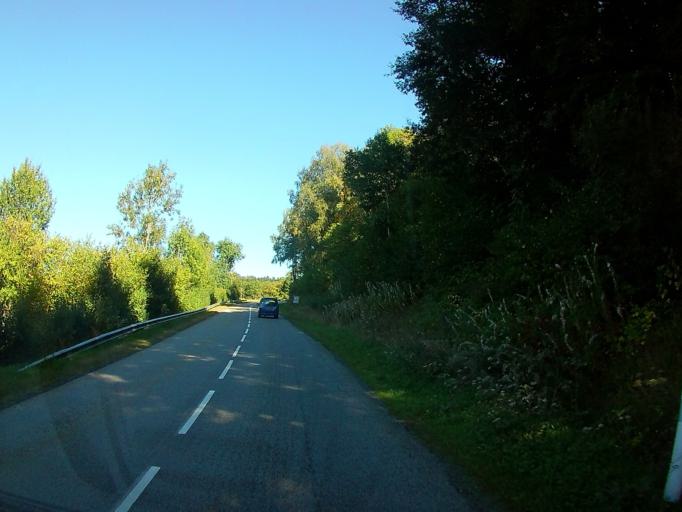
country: FR
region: Auvergne
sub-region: Departement du Puy-de-Dome
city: Saint-Ours
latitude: 45.8724
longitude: 2.8860
